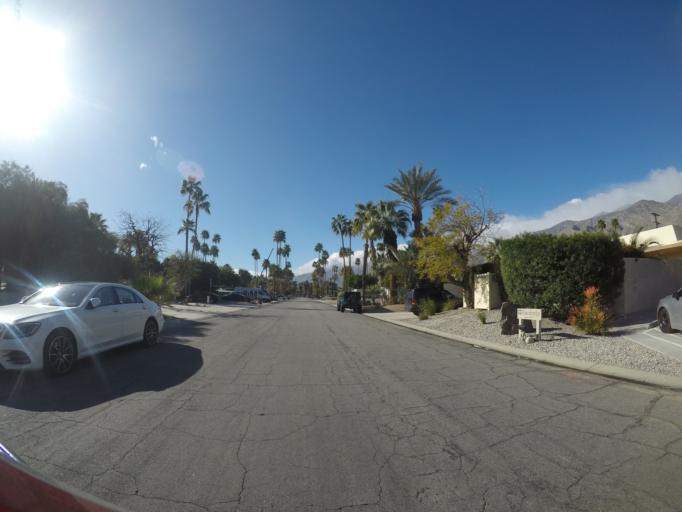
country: US
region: California
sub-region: Riverside County
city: Palm Springs
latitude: 33.8147
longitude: -116.5353
